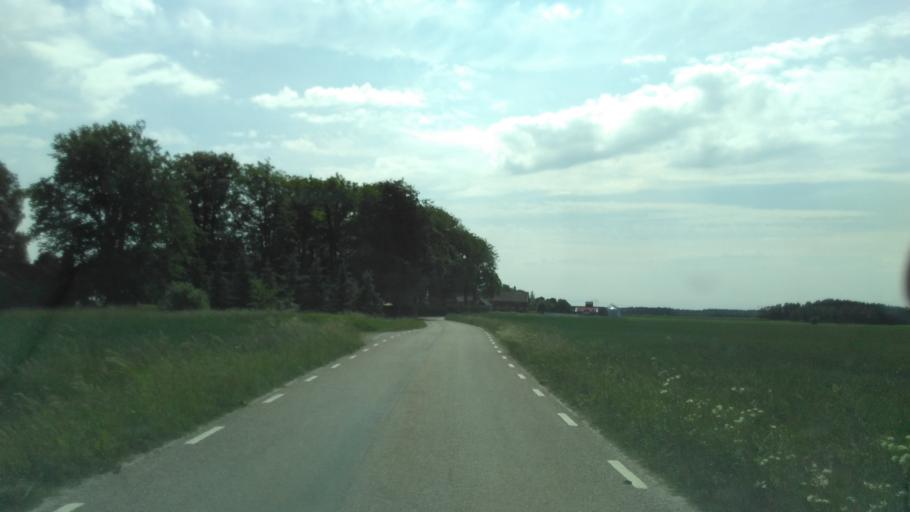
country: SE
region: Vaestra Goetaland
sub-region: Grastorps Kommun
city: Graestorp
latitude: 58.3918
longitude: 12.7923
